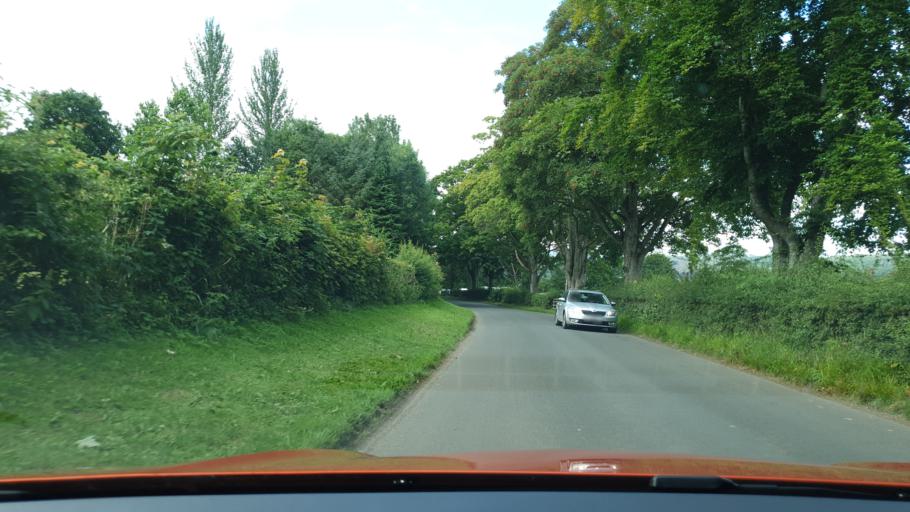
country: GB
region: England
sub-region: Cumbria
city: Penrith
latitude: 54.6058
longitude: -2.8214
